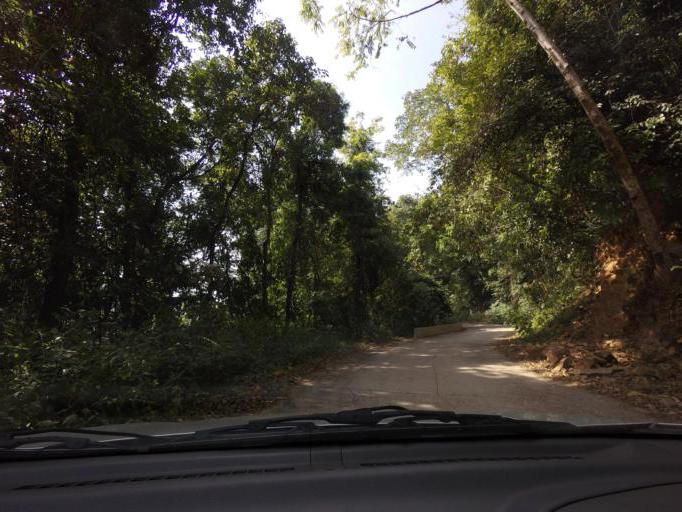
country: IN
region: Karnataka
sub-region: Kodagu
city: Somvarpet
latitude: 12.7145
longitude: 75.6534
